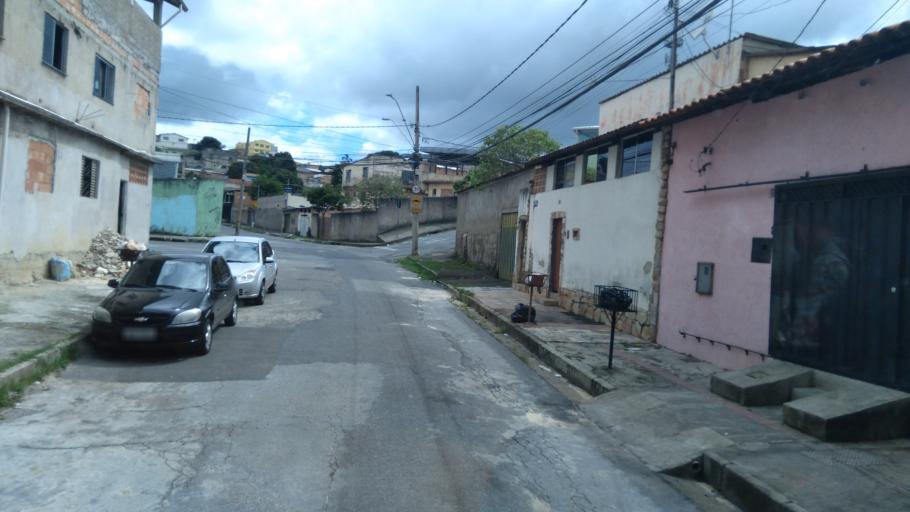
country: BR
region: Minas Gerais
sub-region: Belo Horizonte
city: Belo Horizonte
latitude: -19.8882
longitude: -43.9014
